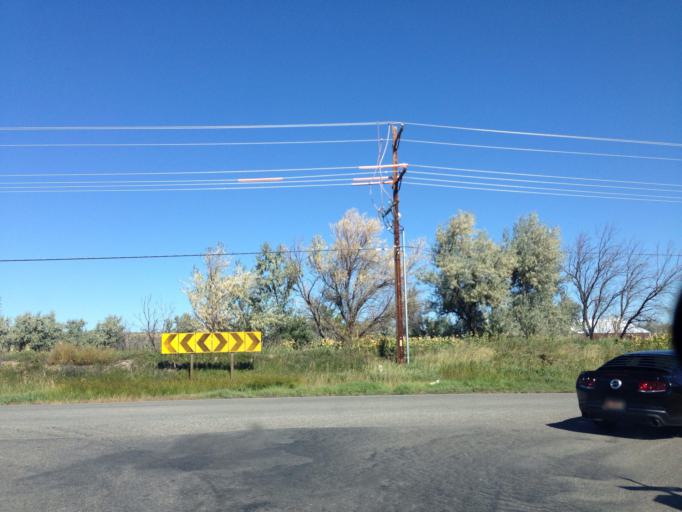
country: US
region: Montana
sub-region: Yellowstone County
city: Laurel
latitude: 45.7838
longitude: -108.6797
